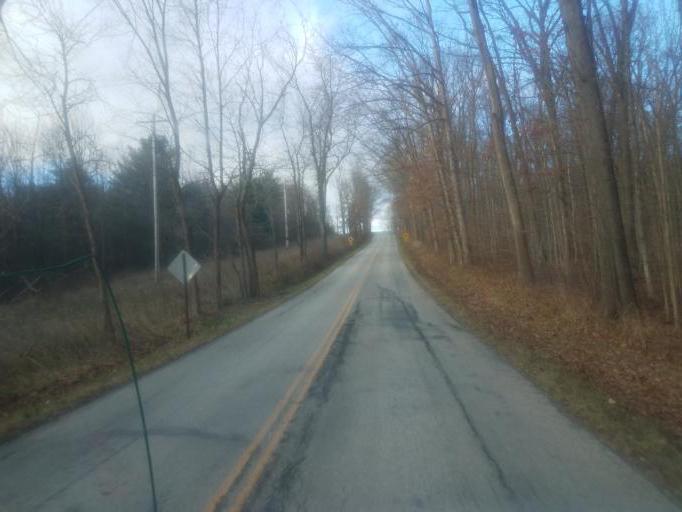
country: US
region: Ohio
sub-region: Sandusky County
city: Bellville
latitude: 40.6026
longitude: -82.3767
